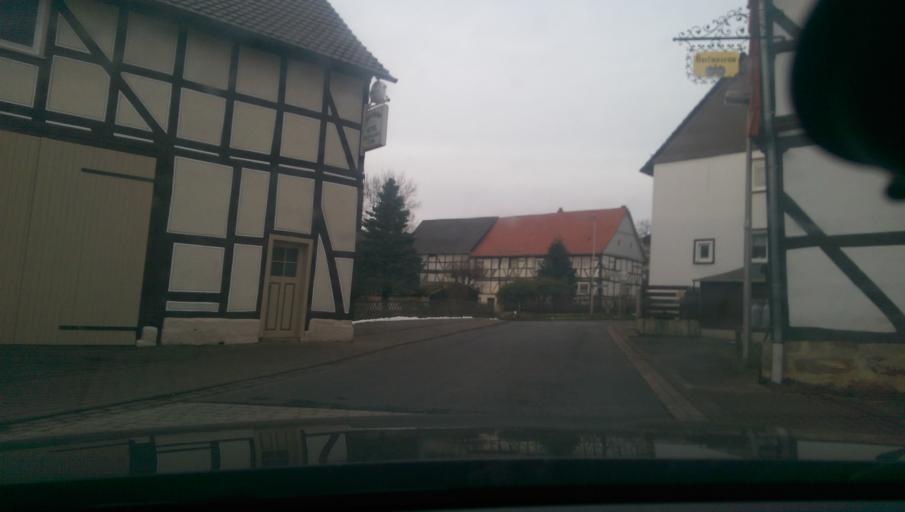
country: DE
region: Hesse
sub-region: Regierungsbezirk Kassel
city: Nieste
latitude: 51.3425
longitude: 9.6618
